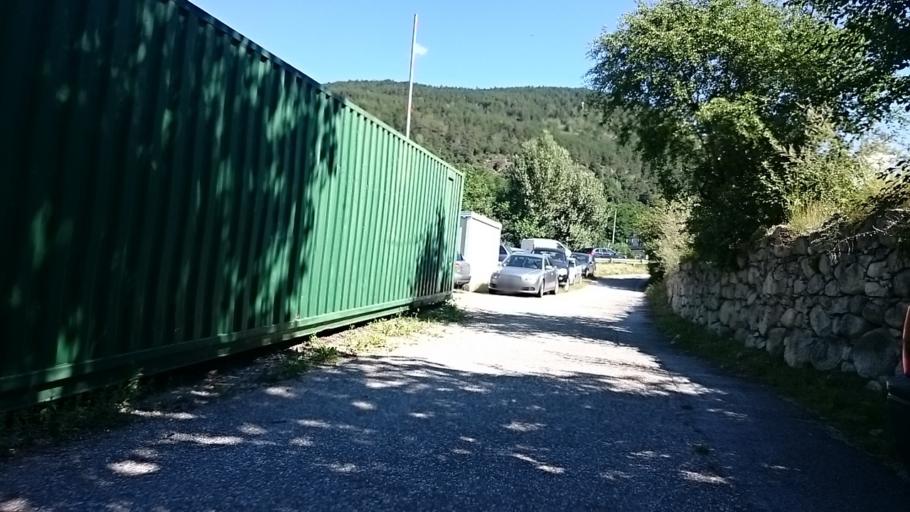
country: IT
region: Trentino-Alto Adige
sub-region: Bolzano
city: Naz-Sciaves - Natz-Schabs
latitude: 46.7696
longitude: 11.6558
